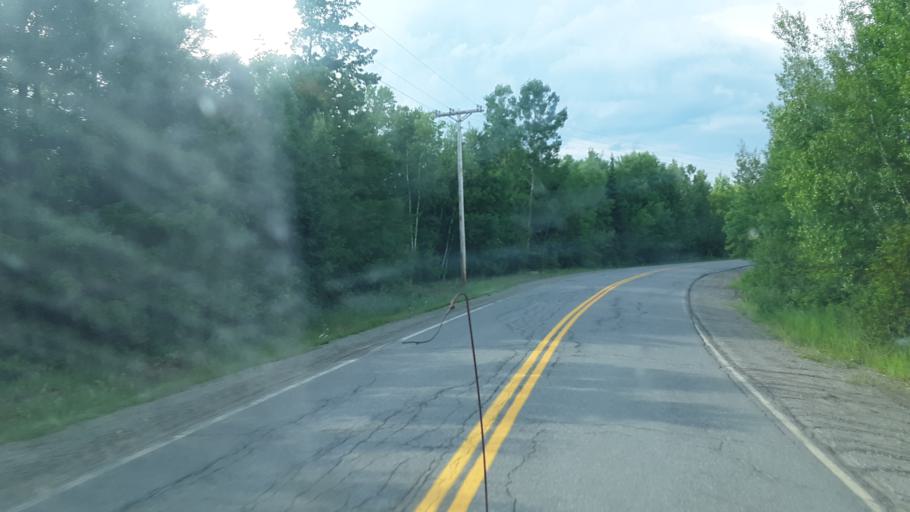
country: US
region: Maine
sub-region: Washington County
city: Calais
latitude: 45.1126
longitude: -67.5067
